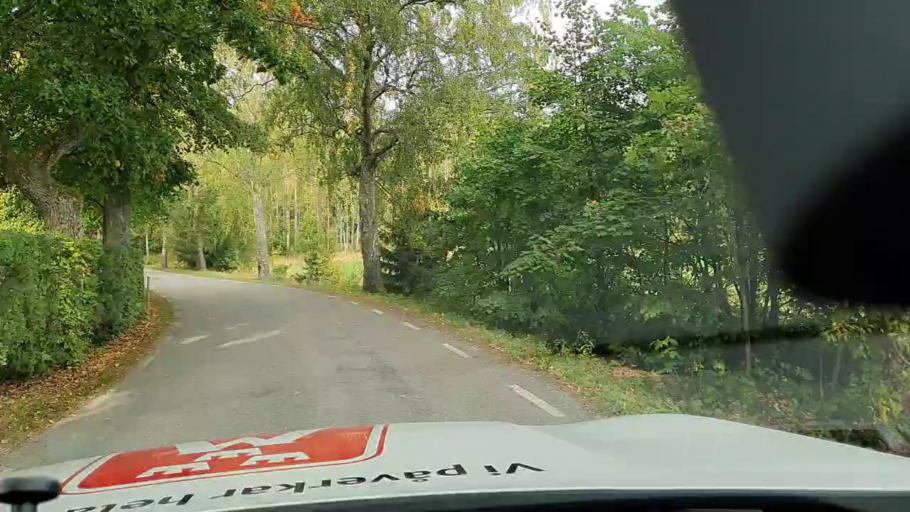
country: SE
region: Soedermanland
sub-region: Nykopings Kommun
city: Svalsta
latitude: 58.8297
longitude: 16.8830
